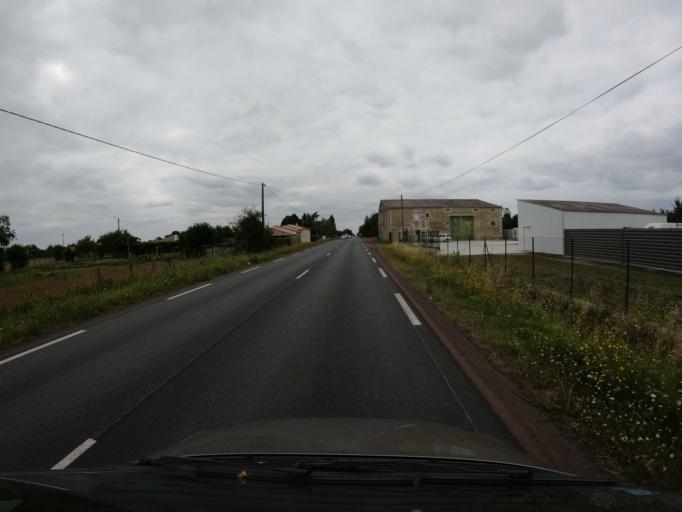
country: FR
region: Pays de la Loire
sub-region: Departement de la Vendee
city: Saint-Michel-le-Cloucq
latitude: 46.4345
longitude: -0.7372
